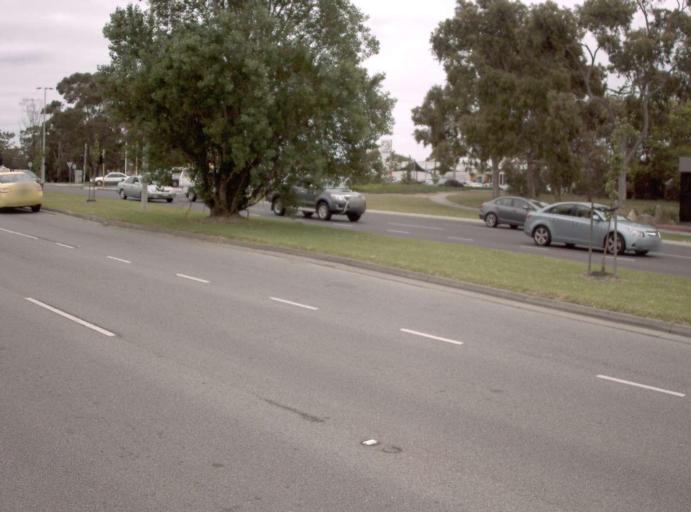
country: AU
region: Victoria
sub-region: Mornington Peninsula
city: Mornington
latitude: -38.2291
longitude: 145.0457
